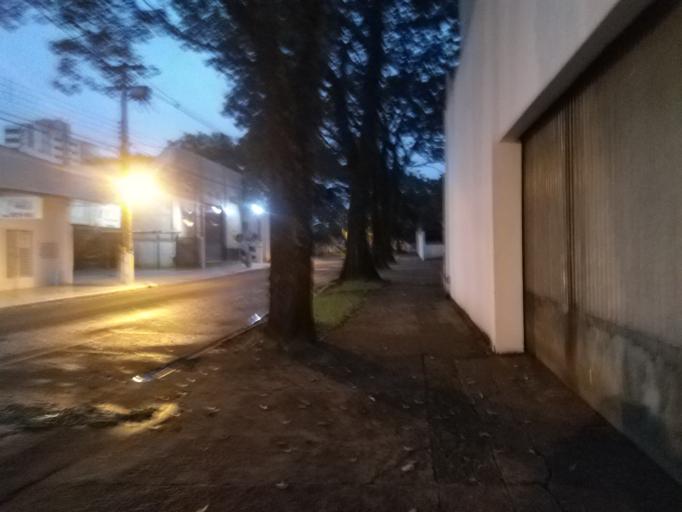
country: BR
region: Parana
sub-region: Maringa
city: Maringa
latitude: -23.4128
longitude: -51.9307
